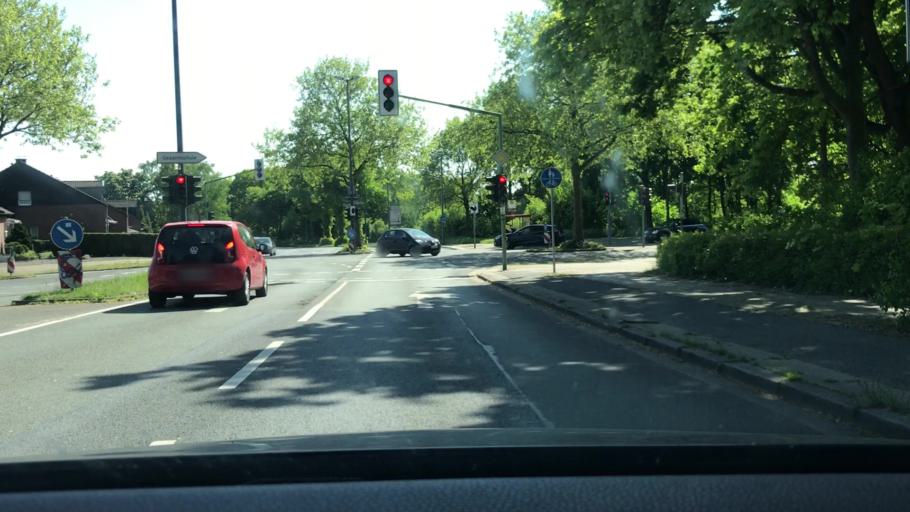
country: DE
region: North Rhine-Westphalia
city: Herten
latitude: 51.6095
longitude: 7.1440
